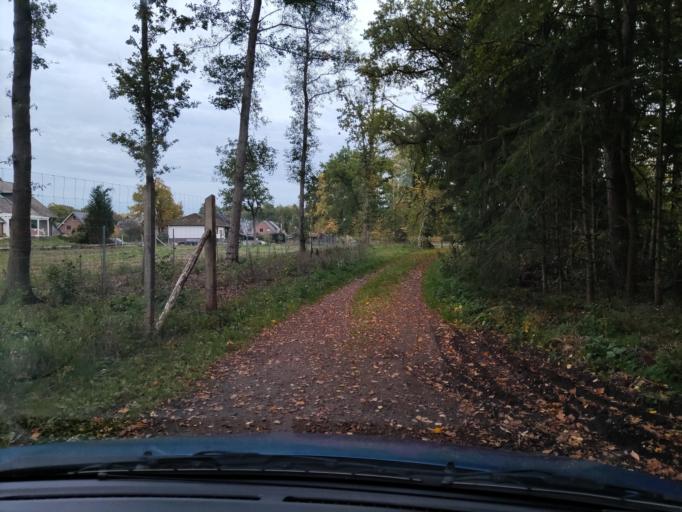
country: DE
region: Lower Saxony
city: Hermannsburg
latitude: 52.8676
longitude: 10.1226
